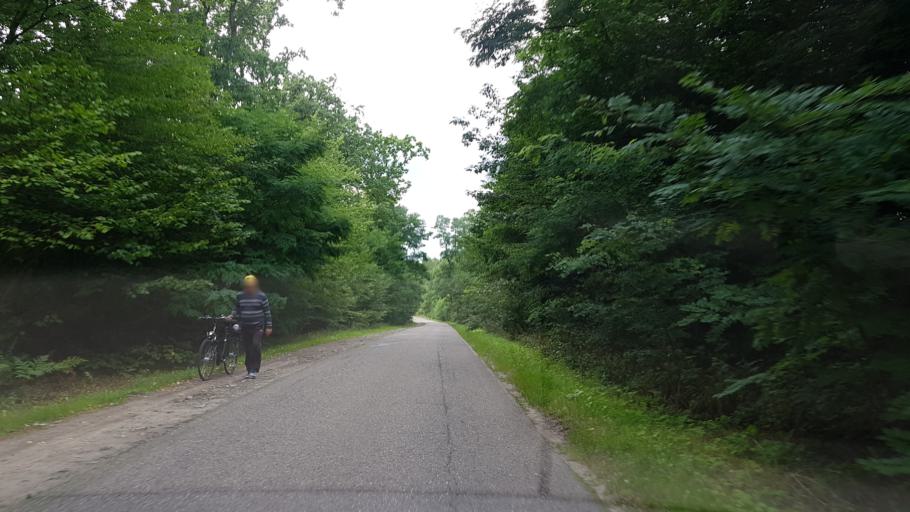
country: PL
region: West Pomeranian Voivodeship
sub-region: Powiat bialogardzki
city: Tychowo
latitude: 54.0272
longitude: 16.3549
